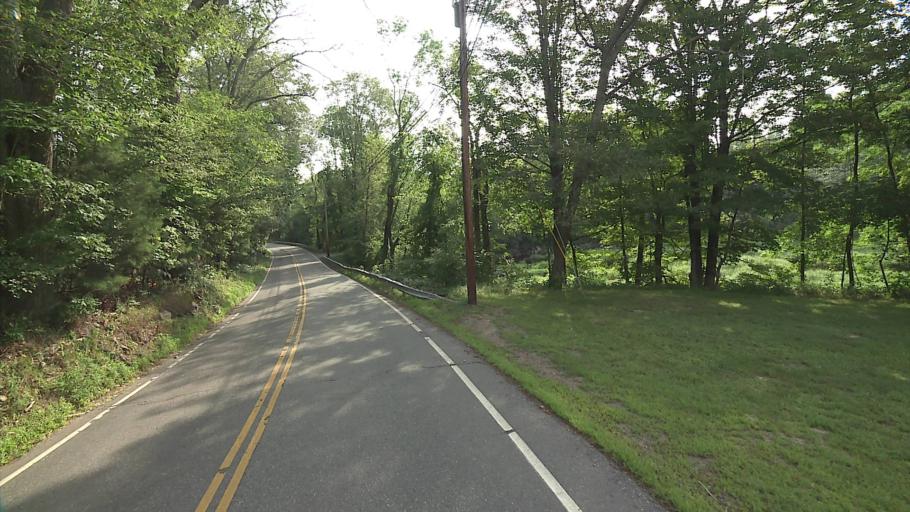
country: US
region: Connecticut
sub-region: Windham County
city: Quinebaug
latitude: 41.9944
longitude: -71.9929
